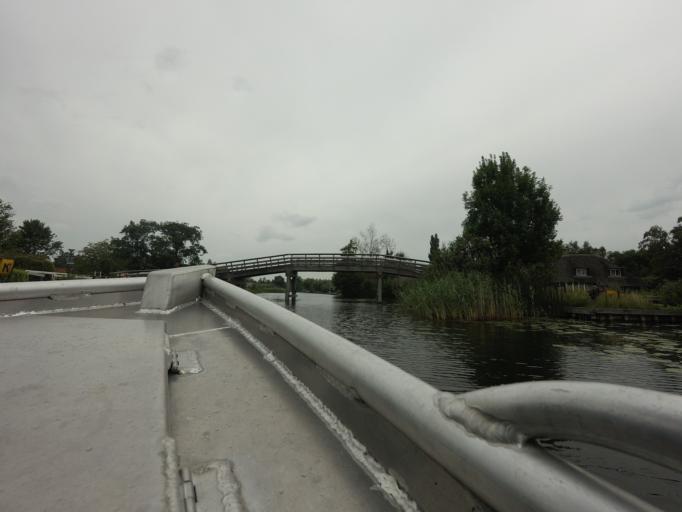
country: NL
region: Overijssel
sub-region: Gemeente Steenwijkerland
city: Giethoorn
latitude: 52.7201
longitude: 6.0394
